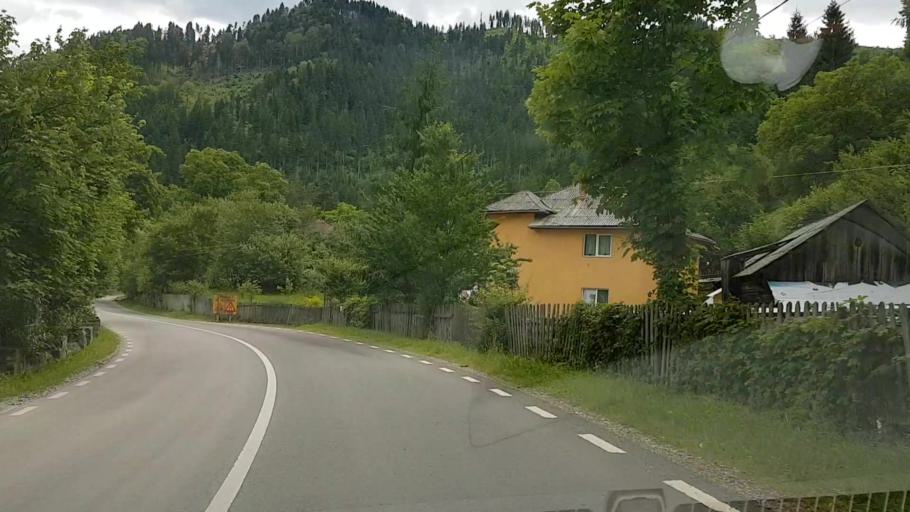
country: RO
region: Neamt
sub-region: Comuna Poiana Teiului
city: Poiana Teiului
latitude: 47.0960
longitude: 25.9425
